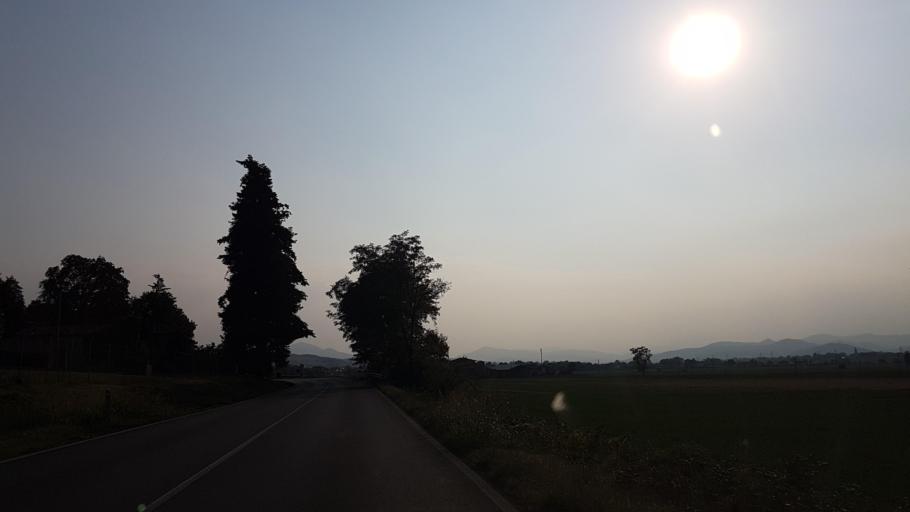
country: IT
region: Emilia-Romagna
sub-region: Provincia di Parma
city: Gaiano
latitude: 44.7326
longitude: 10.1851
